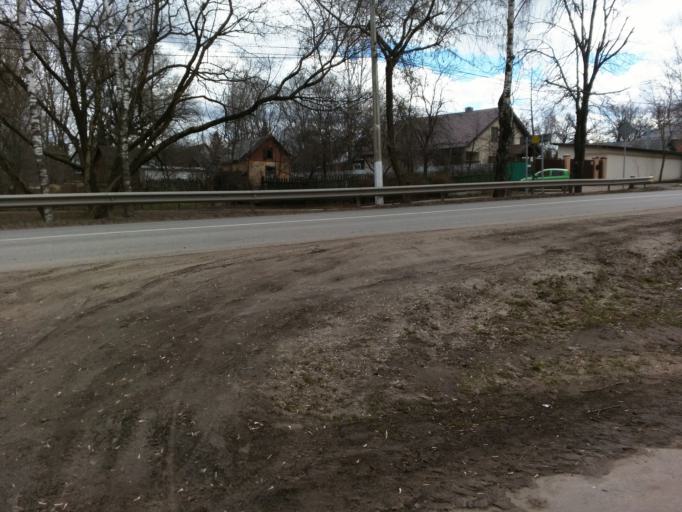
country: RU
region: Moskovskaya
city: Saltykovka
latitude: 55.7705
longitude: 37.9263
